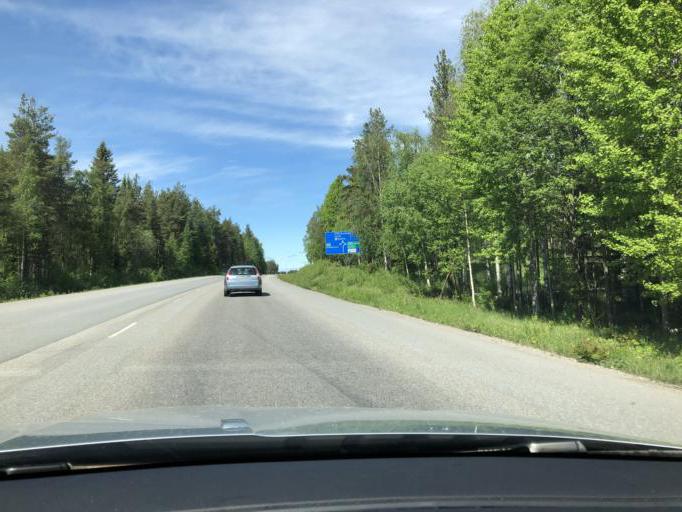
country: SE
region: Norrbotten
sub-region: Pitea Kommun
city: Pitea
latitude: 65.3272
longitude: 21.4311
